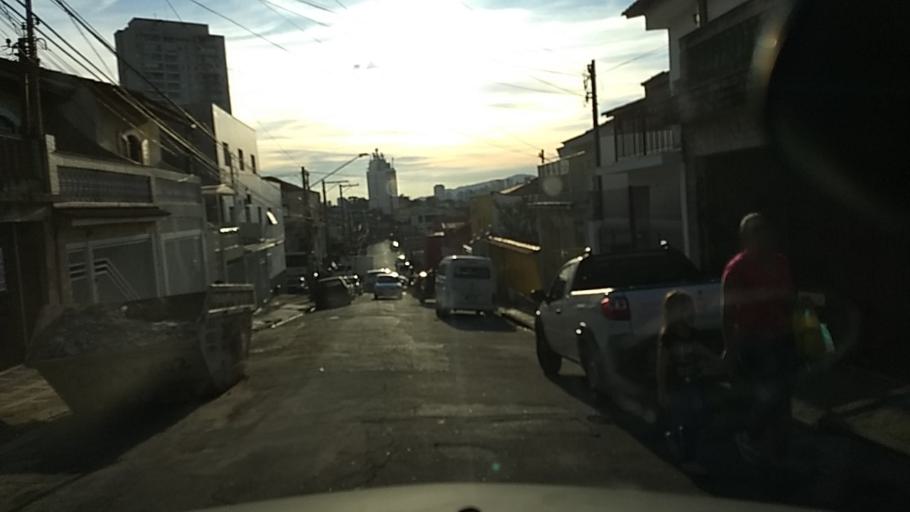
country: BR
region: Sao Paulo
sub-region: Sao Paulo
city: Sao Paulo
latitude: -23.4983
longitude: -46.5943
